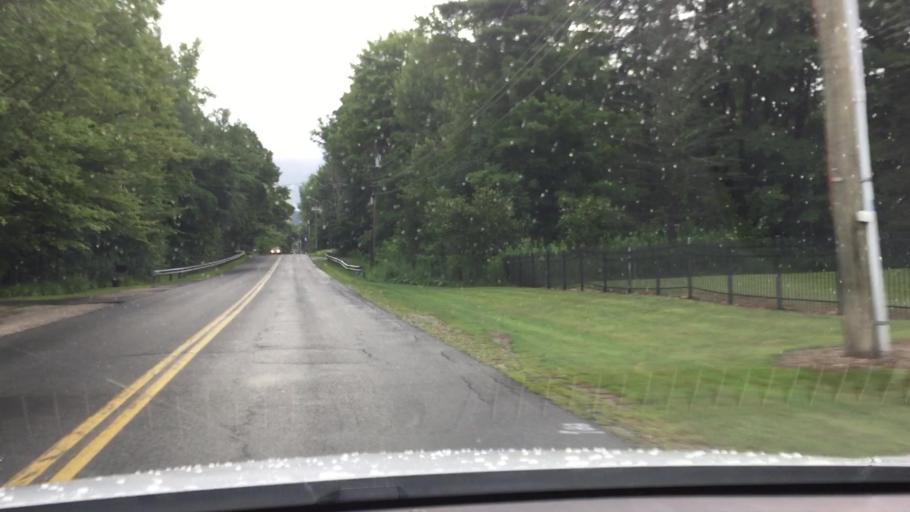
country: US
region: Massachusetts
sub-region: Berkshire County
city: Dalton
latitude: 42.4449
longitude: -73.1930
